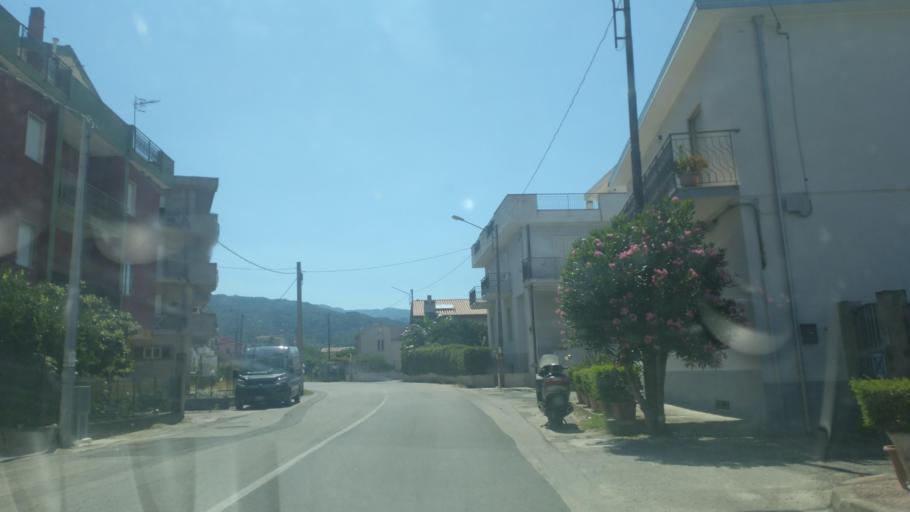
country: IT
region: Calabria
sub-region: Provincia di Catanzaro
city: Marina di Davoli
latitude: 38.6677
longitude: 16.5414
